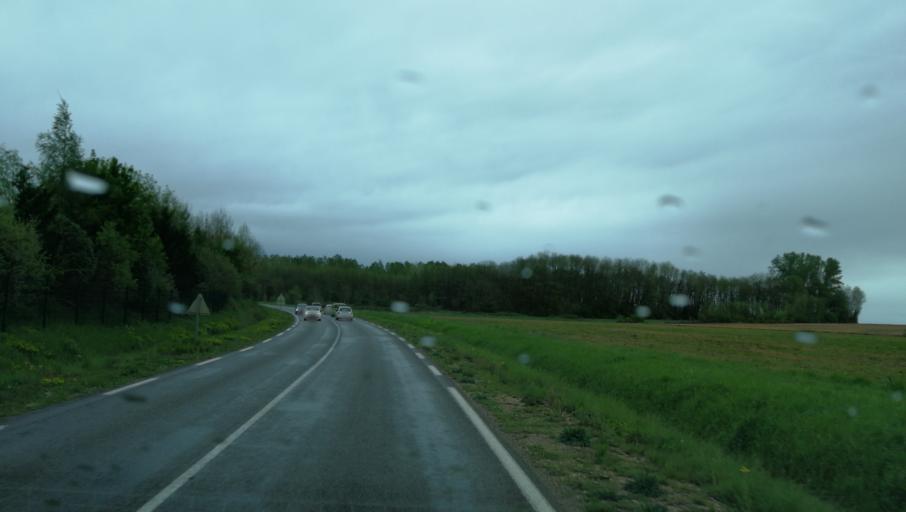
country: FR
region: Franche-Comte
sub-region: Departement du Jura
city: Bletterans
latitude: 46.7163
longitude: 5.4743
